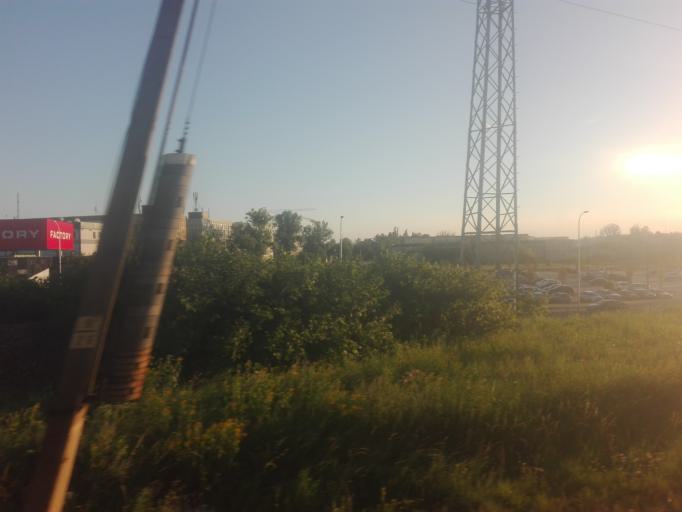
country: PL
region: Masovian Voivodeship
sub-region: Warszawa
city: Ursus
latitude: 52.2039
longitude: 20.8942
